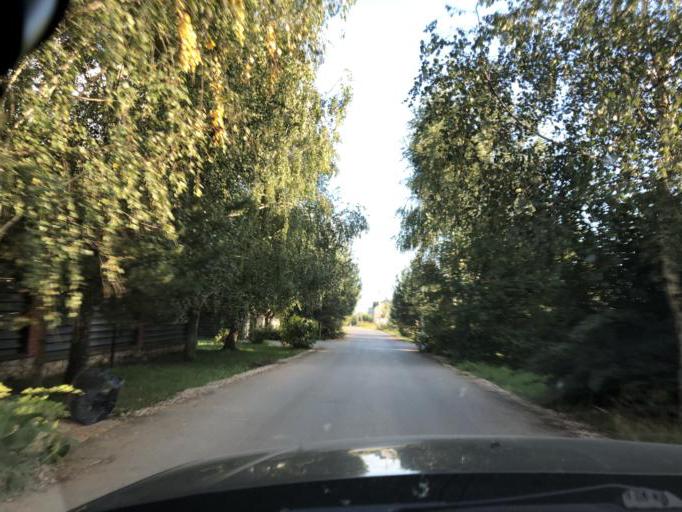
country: RU
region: Tula
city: Kosaya Gora
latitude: 54.1772
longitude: 37.5439
